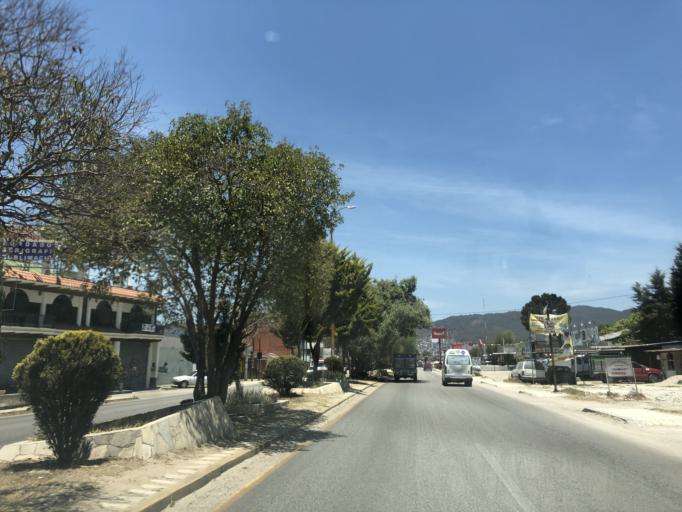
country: MX
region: Chiapas
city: San Cristobal de las Casas
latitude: 16.7233
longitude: -92.6345
